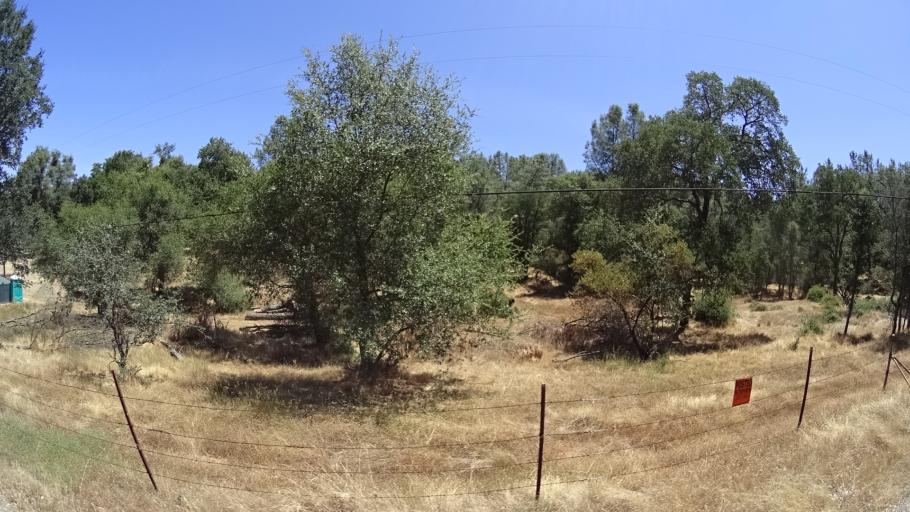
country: US
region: California
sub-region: Calaveras County
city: Valley Springs
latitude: 38.2123
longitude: -120.8620
